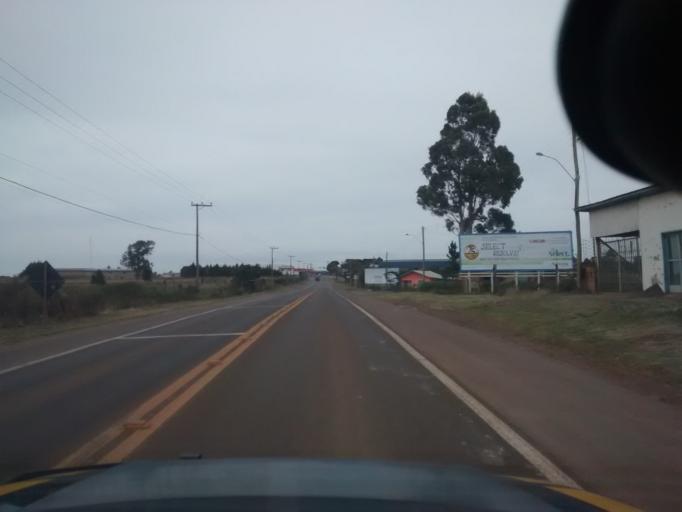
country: BR
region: Rio Grande do Sul
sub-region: Vacaria
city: Vacaria
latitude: -28.4778
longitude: -50.9657
